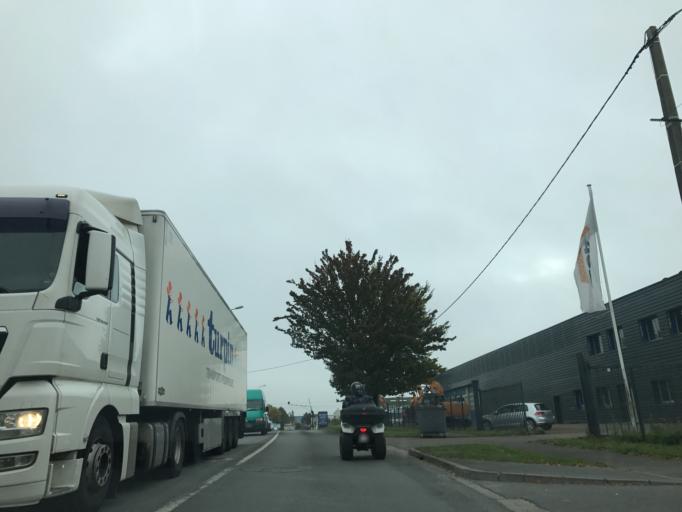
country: FR
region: Nord-Pas-de-Calais
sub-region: Departement du Pas-de-Calais
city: Saint-Laurent-Blangy
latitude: 50.2942
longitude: 2.8049
